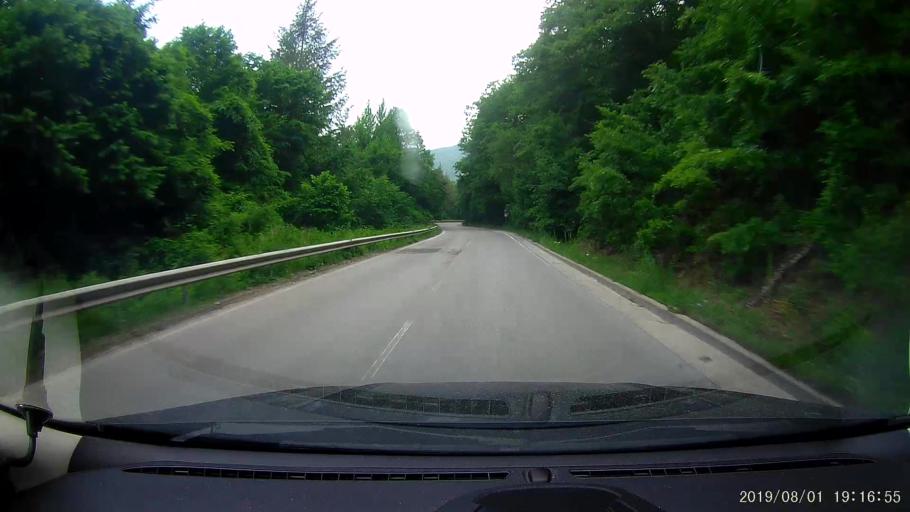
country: BG
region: Shumen
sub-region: Obshtina Smyadovo
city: Smyadovo
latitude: 42.9293
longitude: 26.9471
